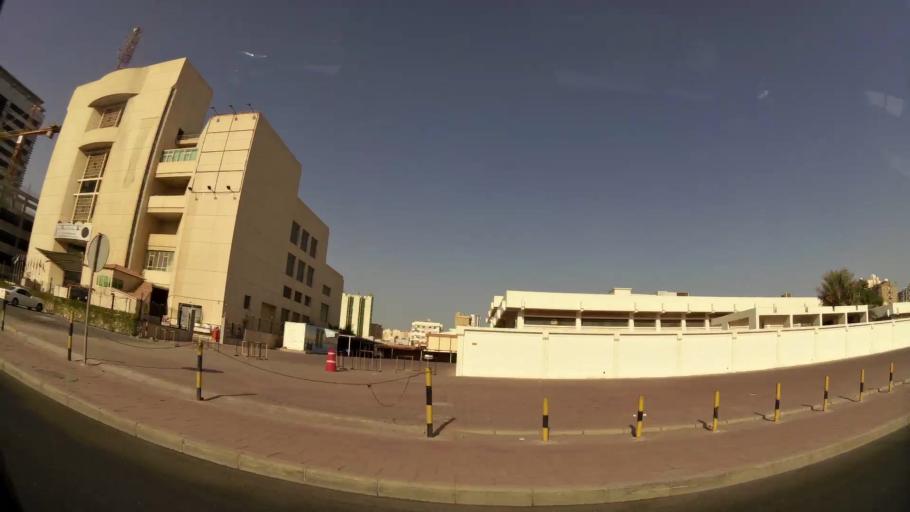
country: KW
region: Muhafazat Hawalli
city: As Salimiyah
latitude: 29.3292
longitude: 48.0823
